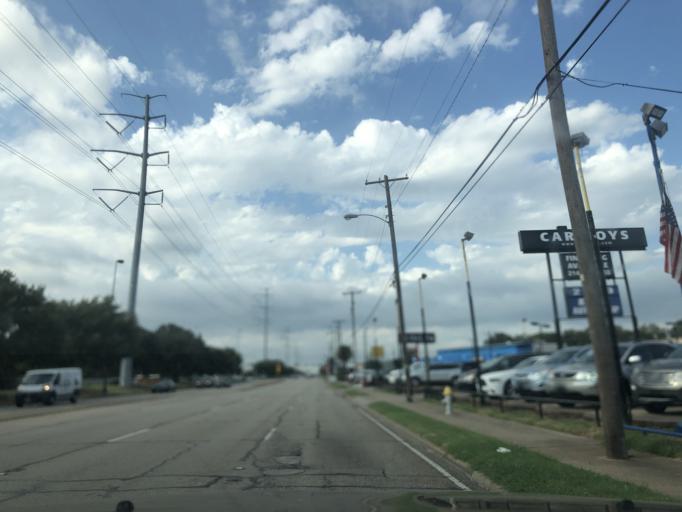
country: US
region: Texas
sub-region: Dallas County
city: Garland
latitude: 32.8809
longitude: -96.6590
